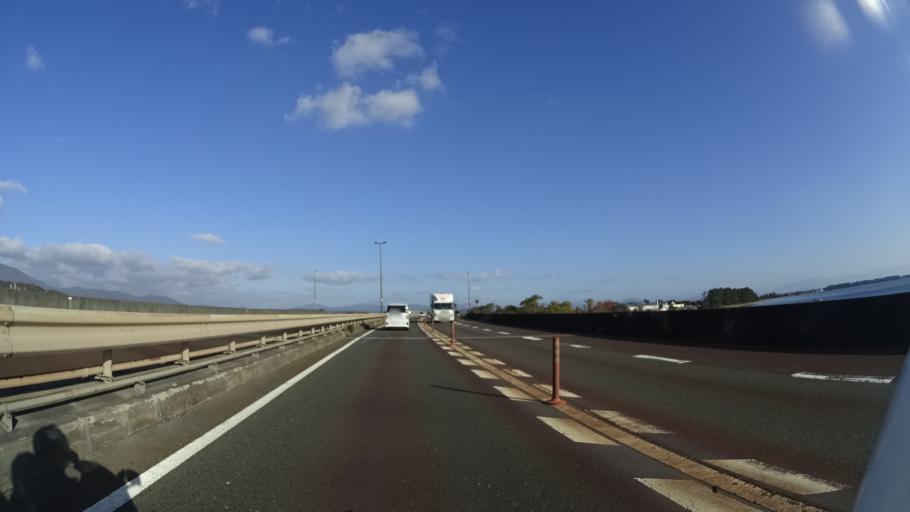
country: JP
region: Shiga Prefecture
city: Kitahama
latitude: 35.2972
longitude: 136.0167
